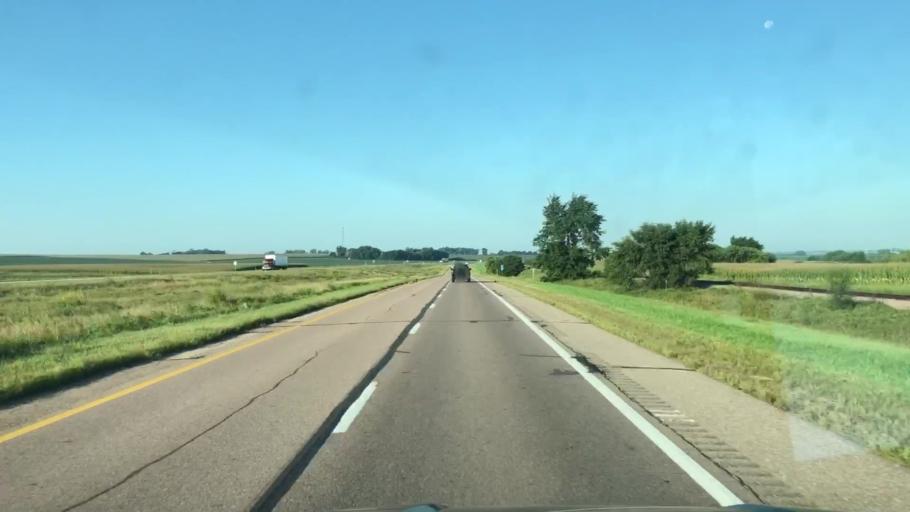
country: US
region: Iowa
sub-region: Sioux County
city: Alton
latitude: 43.0156
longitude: -95.9626
